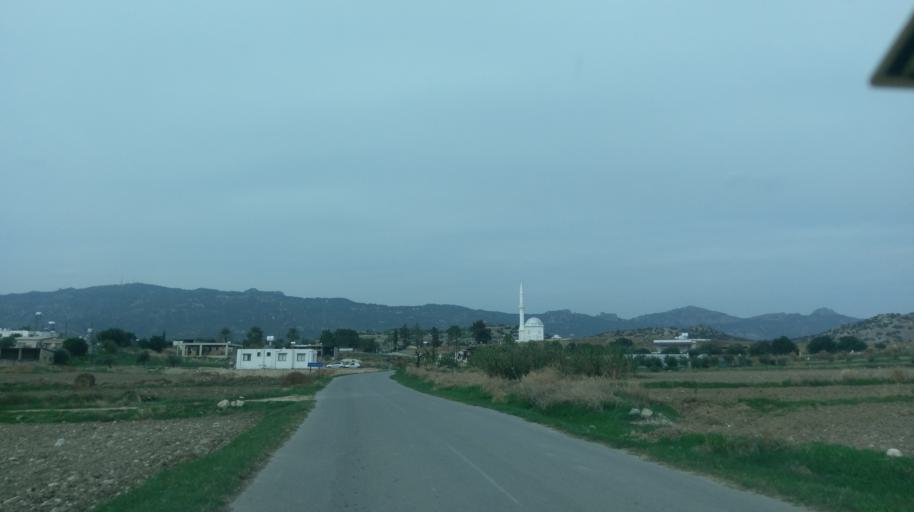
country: CY
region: Ammochostos
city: Trikomo
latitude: 35.3575
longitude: 33.9256
